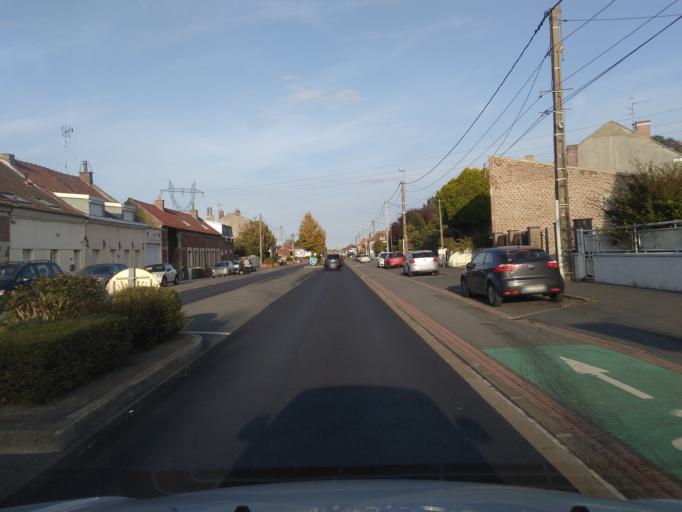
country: FR
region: Nord-Pas-de-Calais
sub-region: Departement du Nord
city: Saint-Saulve
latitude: 50.3765
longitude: 3.5717
